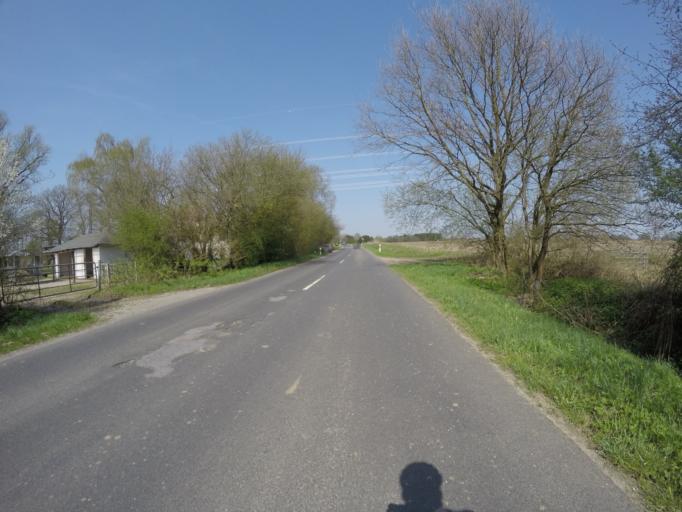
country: DE
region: Schleswig-Holstein
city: Quickborn
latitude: 53.7183
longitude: 9.8860
